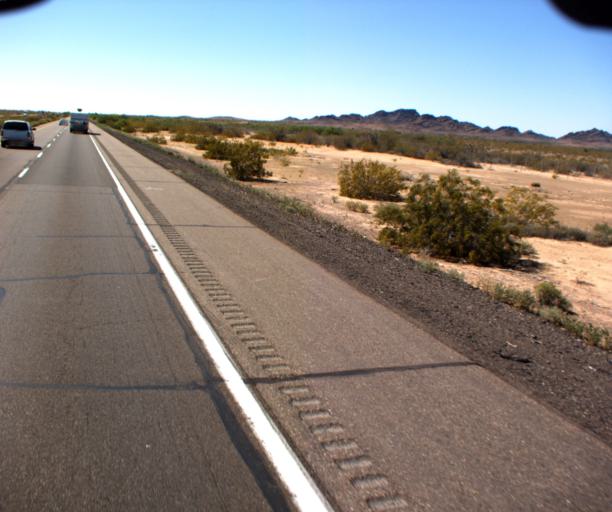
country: US
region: Arizona
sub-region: Maricopa County
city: Gila Bend
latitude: 32.9058
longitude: -112.9879
